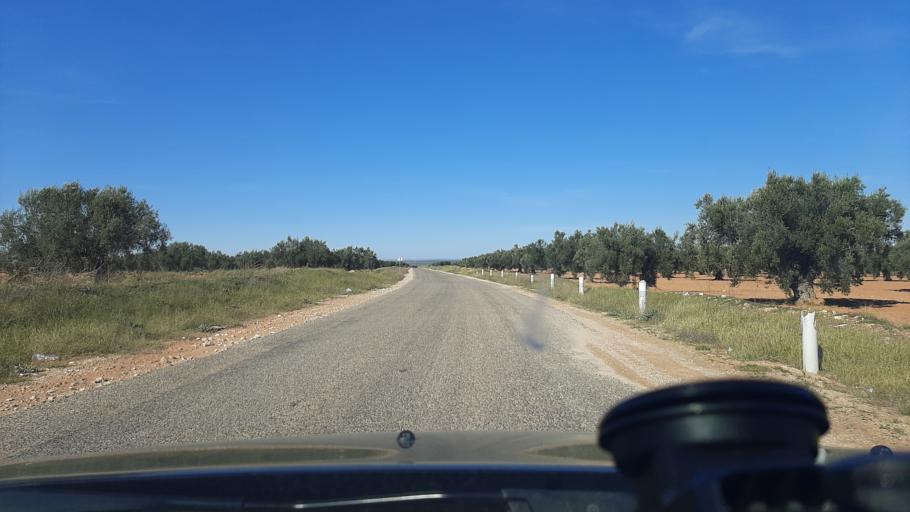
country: TN
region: Safaqis
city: Sfax
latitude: 34.9652
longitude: 10.5380
